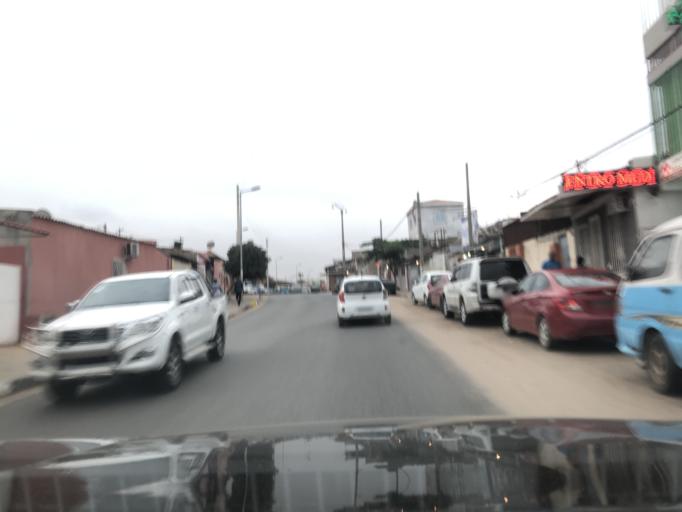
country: AO
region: Luanda
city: Luanda
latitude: -8.8460
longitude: 13.2159
